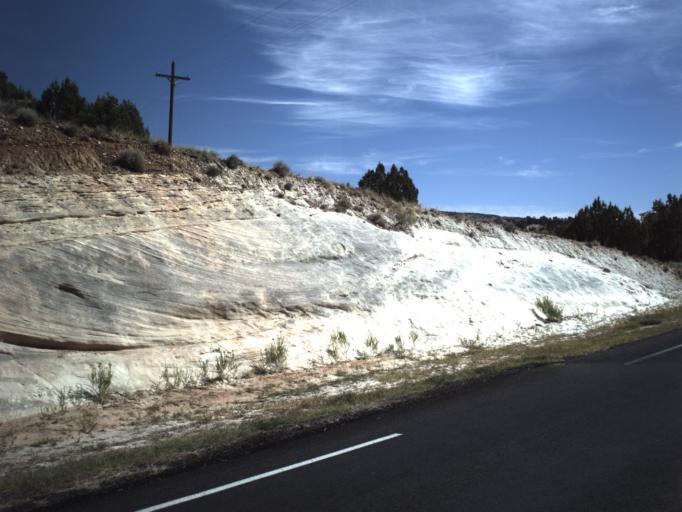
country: US
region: Utah
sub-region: Wayne County
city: Loa
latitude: 37.7746
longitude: -111.6170
